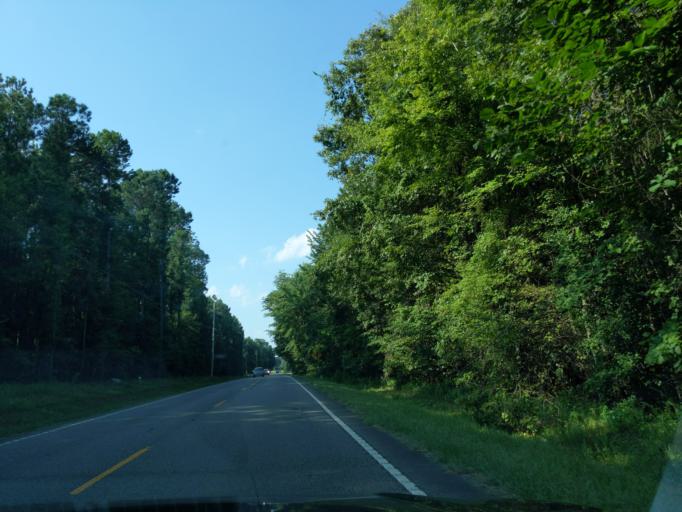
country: US
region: South Carolina
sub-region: Newberry County
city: Prosperity
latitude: 34.0697
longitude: -81.5604
